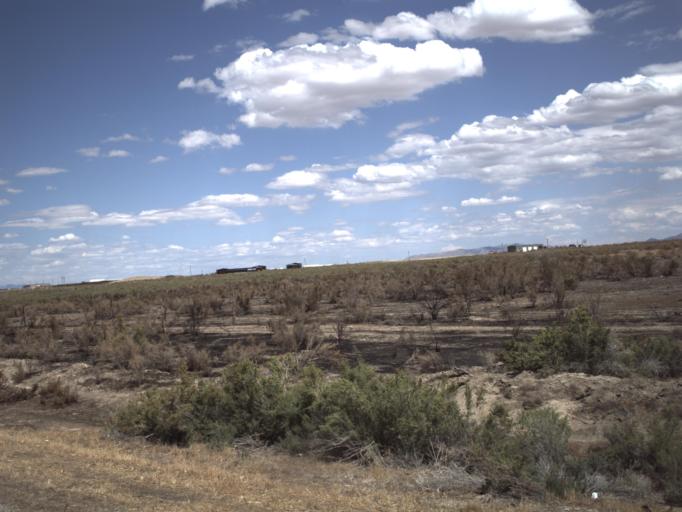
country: US
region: Utah
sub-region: Millard County
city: Delta
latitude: 39.3131
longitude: -112.4781
